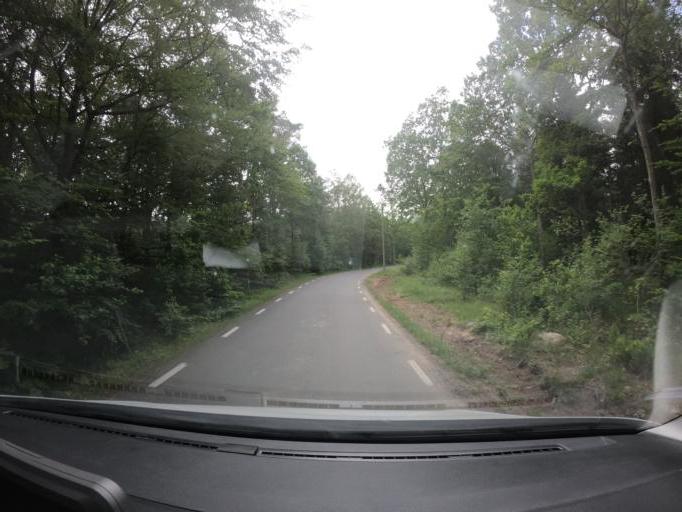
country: SE
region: Skane
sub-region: Hassleholms Kommun
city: Tormestorp
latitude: 56.1232
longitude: 13.6522
